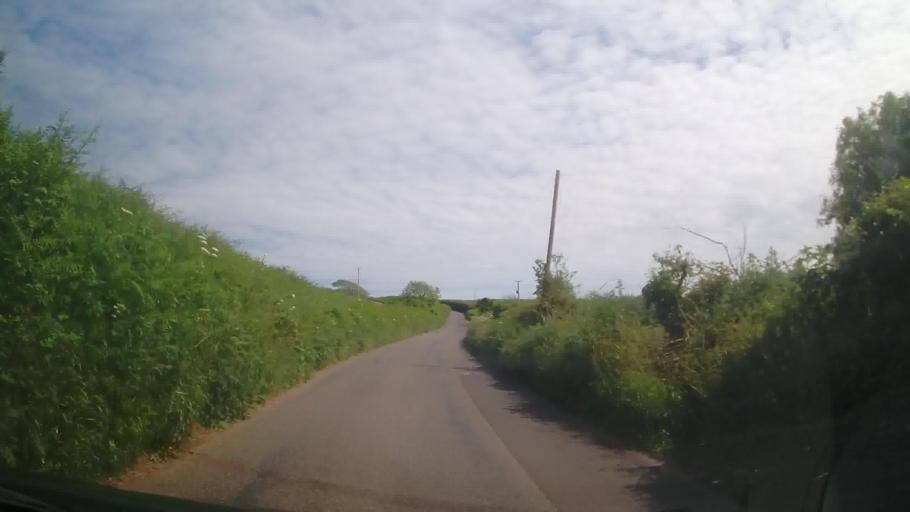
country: GB
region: England
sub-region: Devon
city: Salcombe
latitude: 50.2689
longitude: -3.6791
